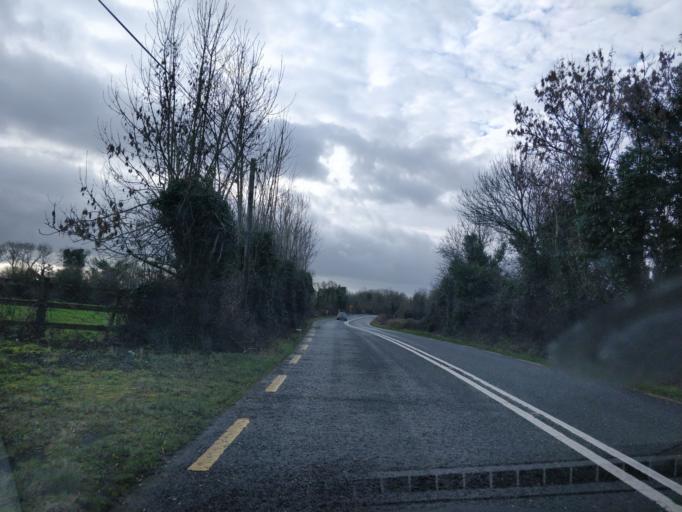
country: IE
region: Connaught
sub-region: Roscommon
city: Roscommon
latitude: 53.7712
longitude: -8.1476
